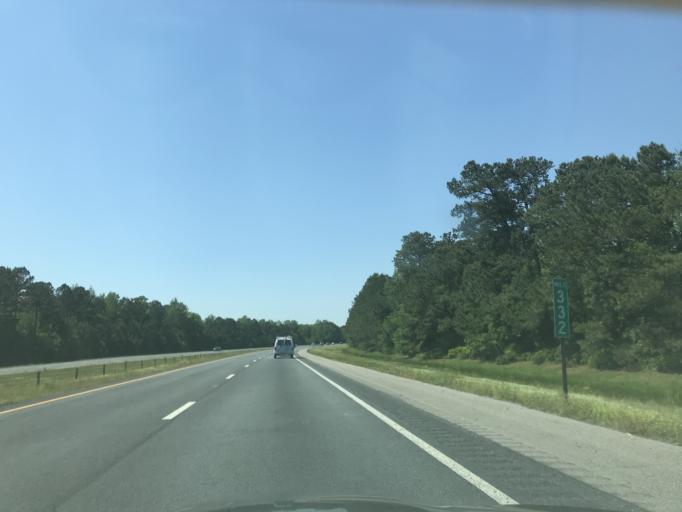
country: US
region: North Carolina
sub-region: Johnston County
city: Benson
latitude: 35.3438
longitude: -78.4710
